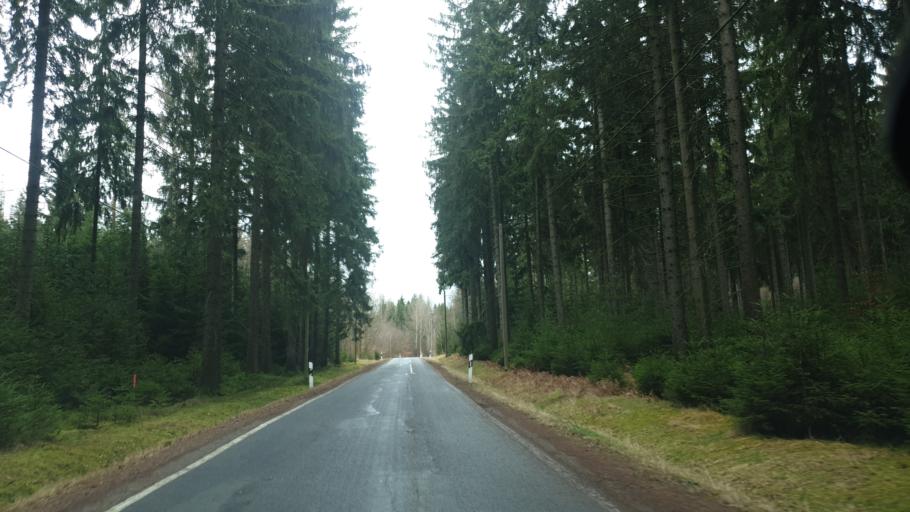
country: CZ
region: Karlovarsky
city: Hranice
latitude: 50.2940
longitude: 12.2007
